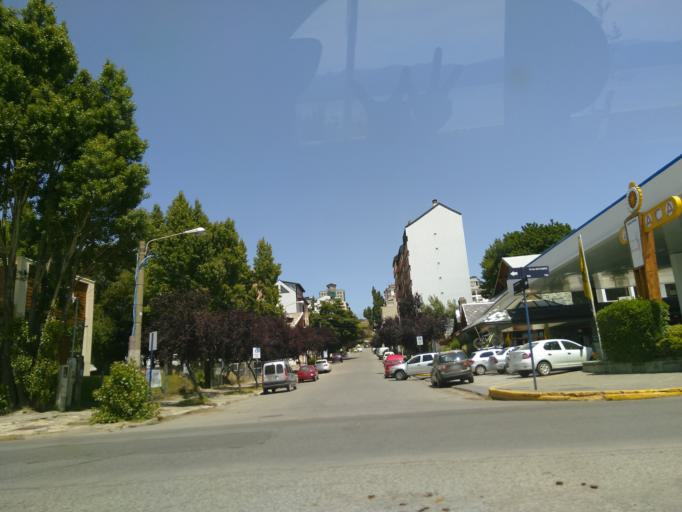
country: AR
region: Rio Negro
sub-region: Departamento de Bariloche
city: San Carlos de Bariloche
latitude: -41.1325
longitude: -71.2979
